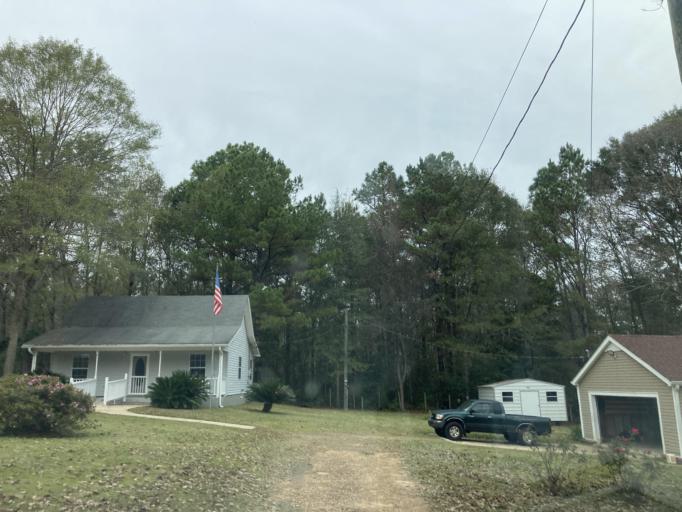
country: US
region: Mississippi
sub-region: Lamar County
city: Purvis
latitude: 31.1105
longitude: -89.4136
